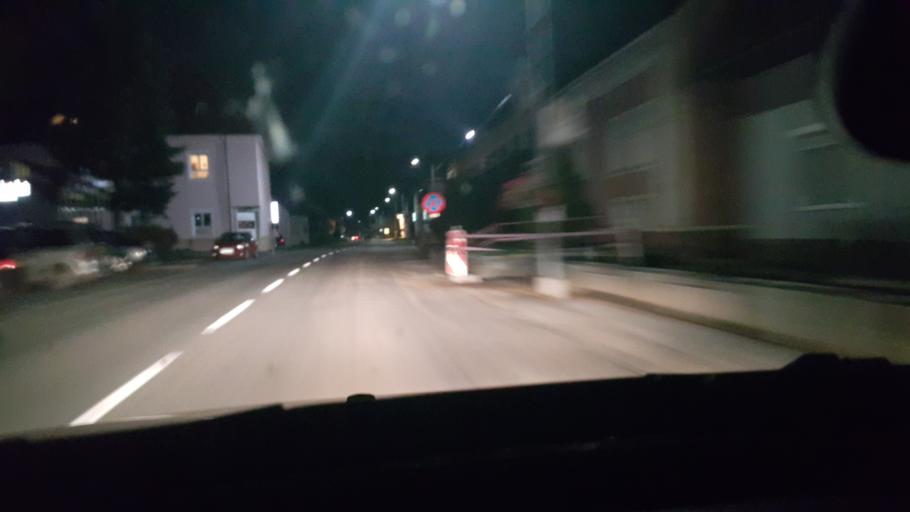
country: AT
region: Styria
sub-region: Politischer Bezirk Deutschlandsberg
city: Sankt Martin im Sulmtal
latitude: 46.7562
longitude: 15.2964
